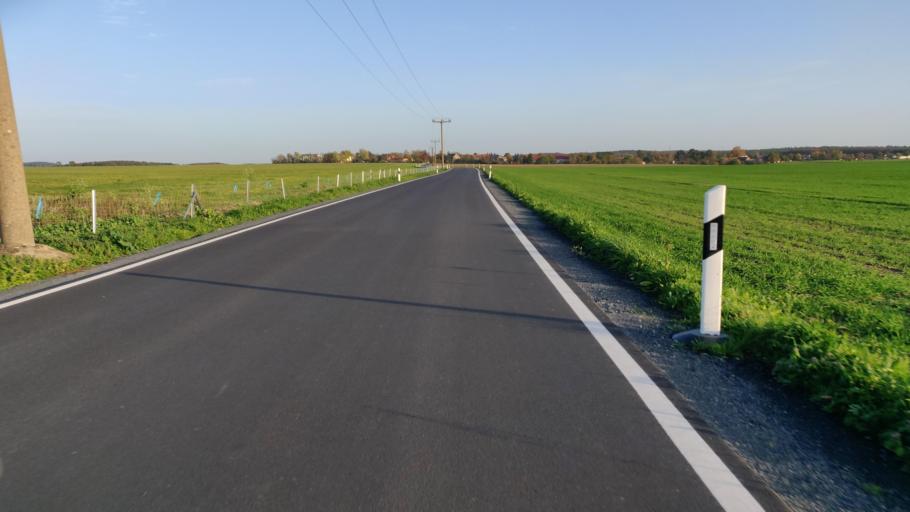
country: DE
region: Brandenburg
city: Hirschfeld
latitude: 51.3507
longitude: 13.6416
